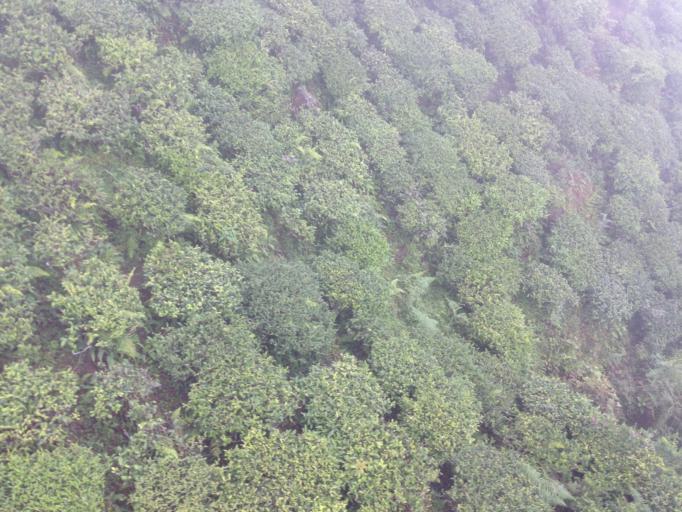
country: IN
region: West Bengal
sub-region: Darjiling
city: Darjiling
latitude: 27.0687
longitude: 88.2545
